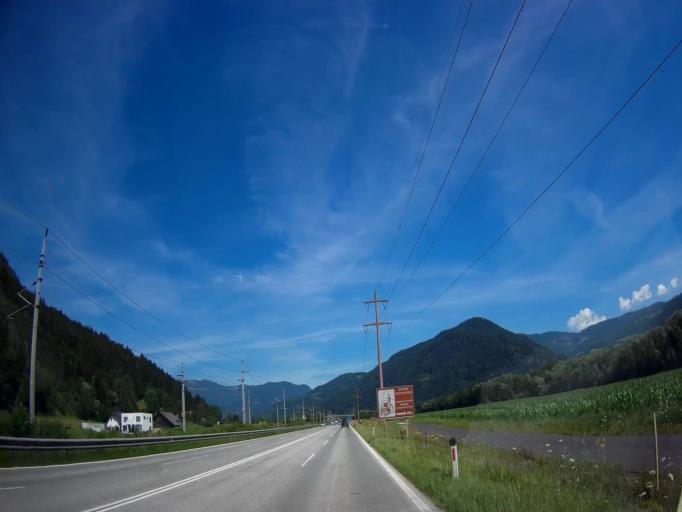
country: AT
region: Carinthia
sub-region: Politischer Bezirk Sankt Veit an der Glan
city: Micheldorf
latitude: 46.9333
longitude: 14.4265
